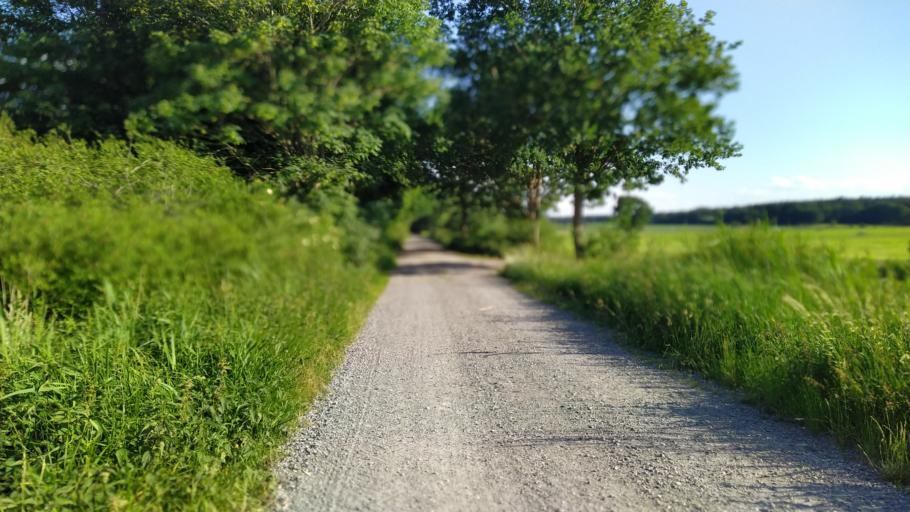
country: DE
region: Lower Saxony
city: Lintig
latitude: 53.5910
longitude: 8.9283
